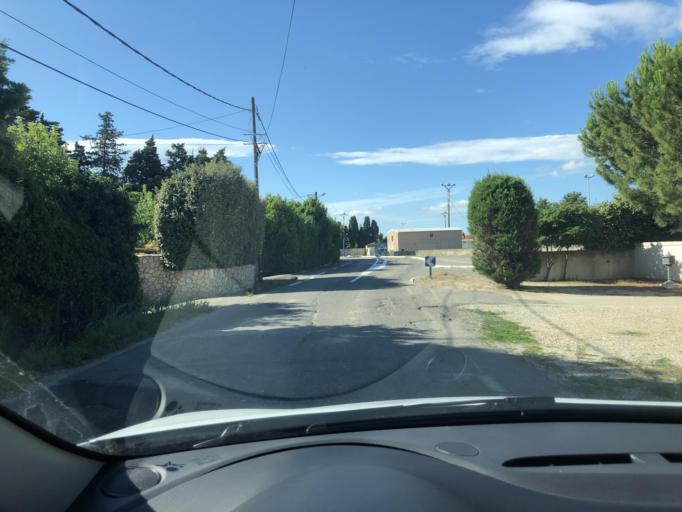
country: FR
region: Provence-Alpes-Cote d'Azur
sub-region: Departement des Bouches-du-Rhone
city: Chateaurenard
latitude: 43.8909
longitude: 4.8461
